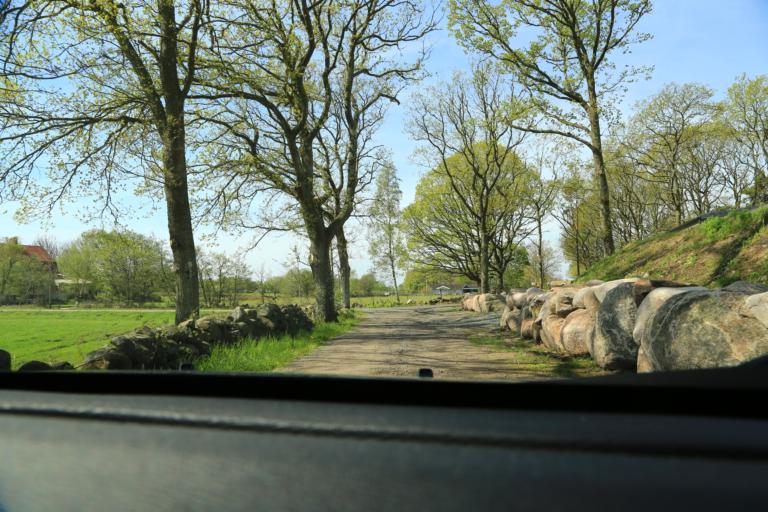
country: SE
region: Halland
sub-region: Varbergs Kommun
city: Varberg
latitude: 57.1398
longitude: 12.2274
